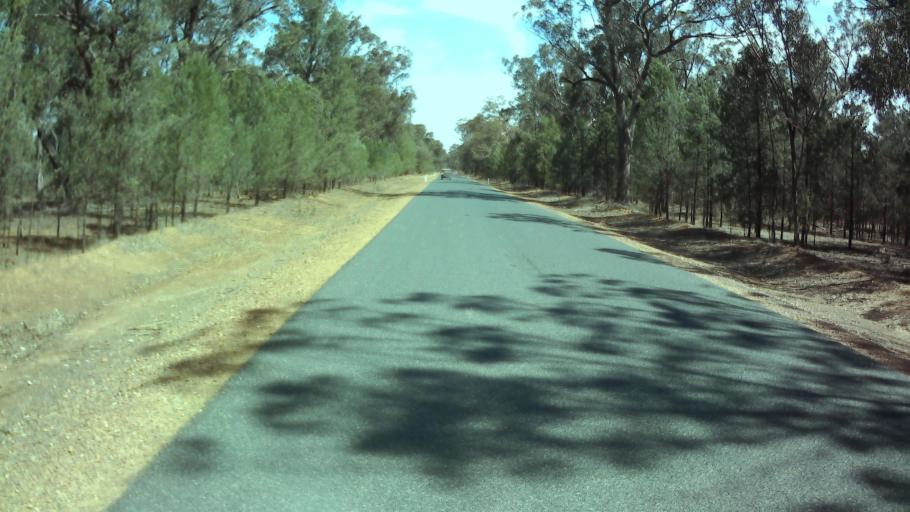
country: AU
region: New South Wales
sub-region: Weddin
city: Grenfell
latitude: -34.0321
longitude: 148.1337
